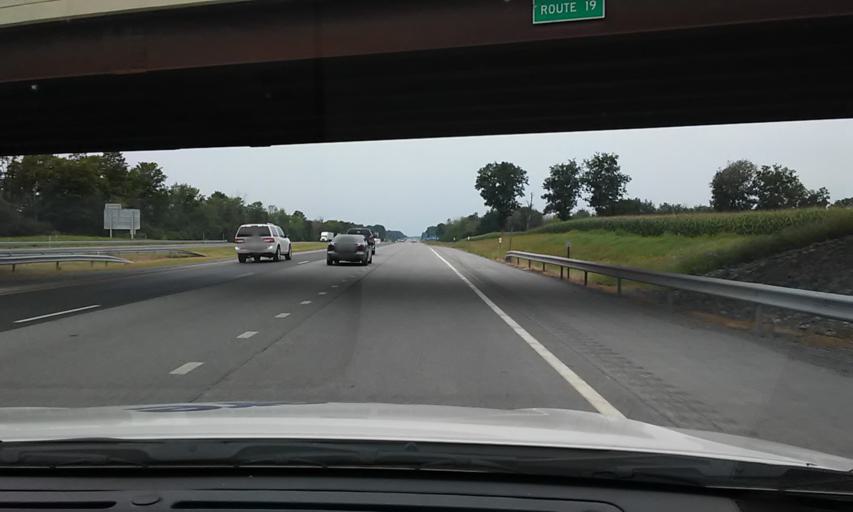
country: US
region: New York
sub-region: Genesee County
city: Le Roy
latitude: 43.0292
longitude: -77.9707
